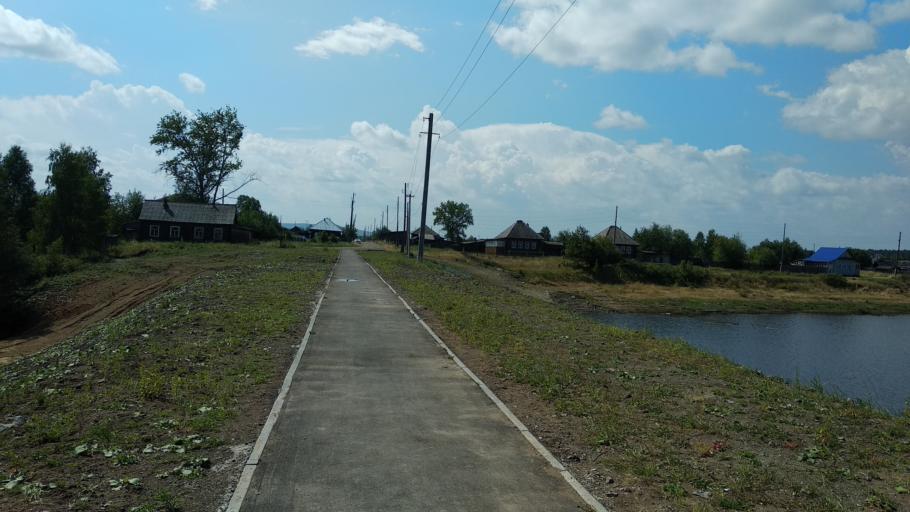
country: RU
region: Sverdlovsk
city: Valerianovsk
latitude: 59.2522
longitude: 59.5005
